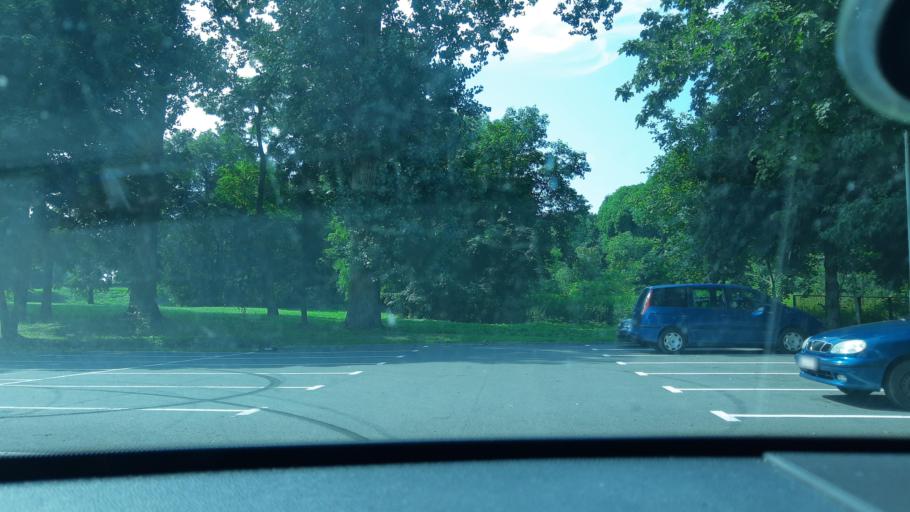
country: PL
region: Lodz Voivodeship
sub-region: Powiat sieradzki
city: Sieradz
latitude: 51.5999
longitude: 18.7404
